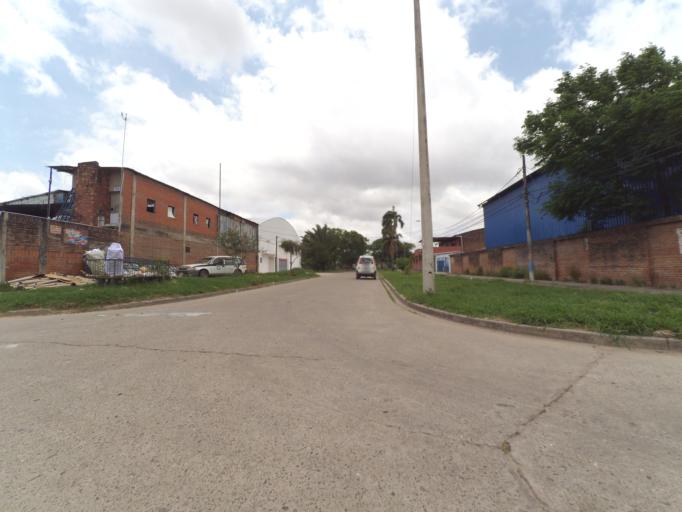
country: BO
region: Santa Cruz
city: Santa Cruz de la Sierra
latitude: -17.7860
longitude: -63.2034
